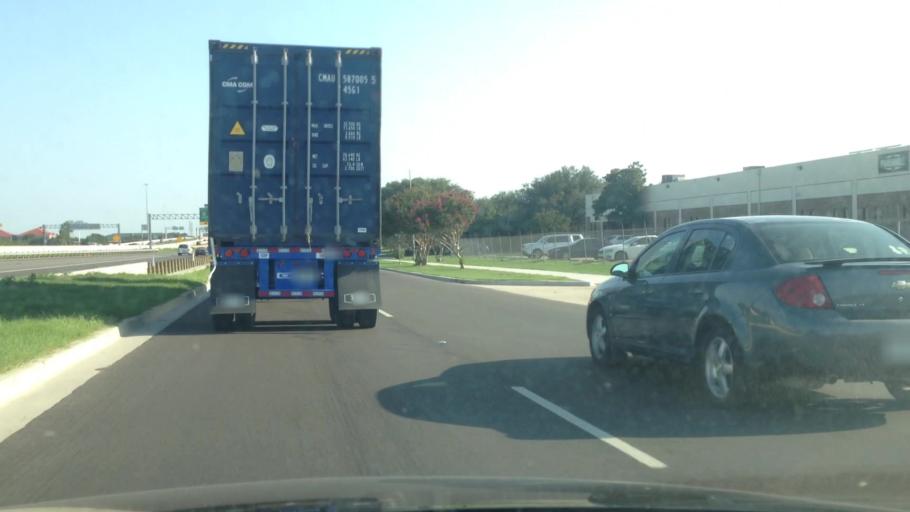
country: US
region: Texas
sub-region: Tarrant County
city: Blue Mound
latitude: 32.8319
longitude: -97.3133
